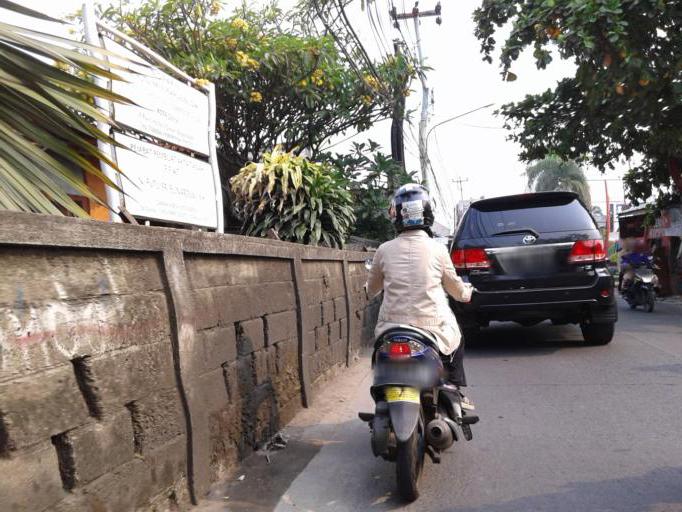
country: ID
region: West Java
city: Pamulang
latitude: -6.3570
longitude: 106.7756
